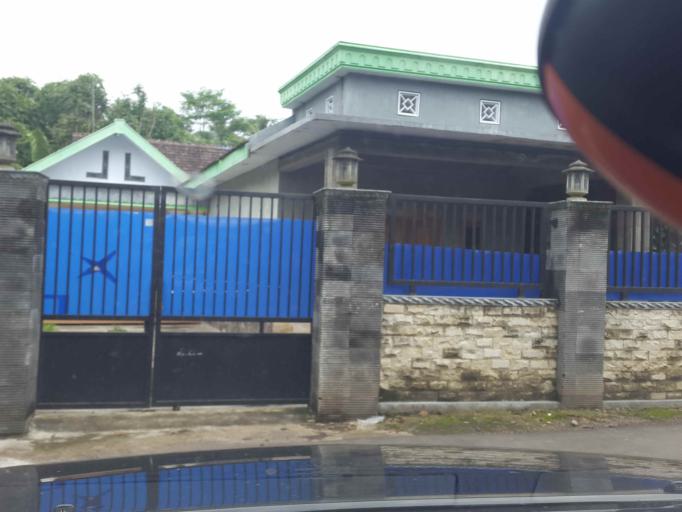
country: ID
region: Central Java
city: Salatiga
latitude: -7.3404
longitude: 110.5147
